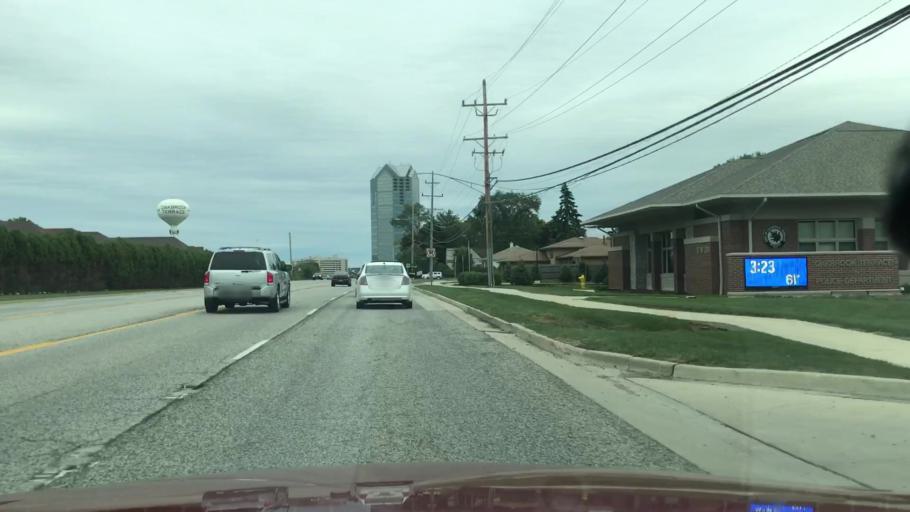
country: US
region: Illinois
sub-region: DuPage County
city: Oakbrook Terrace
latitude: 41.8541
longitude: -87.9651
